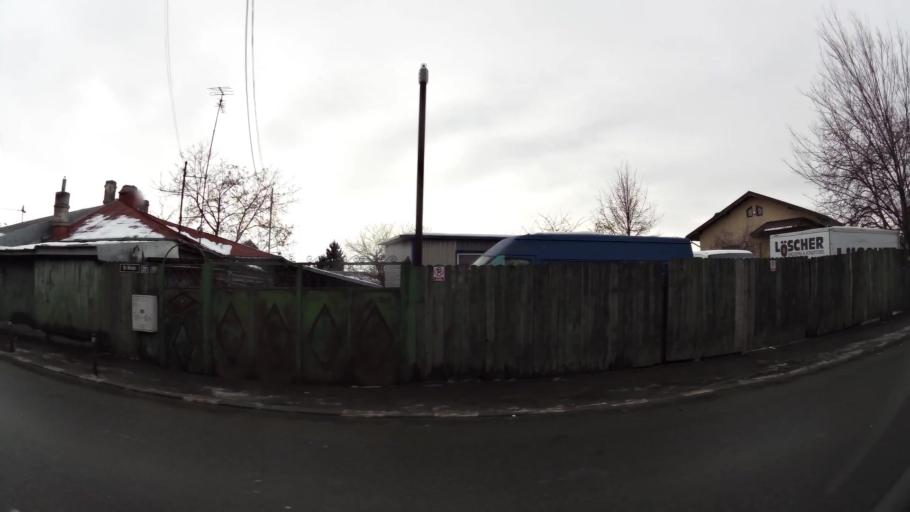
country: RO
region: Ilfov
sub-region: Comuna Pantelimon
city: Pantelimon
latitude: 44.4511
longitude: 26.2068
